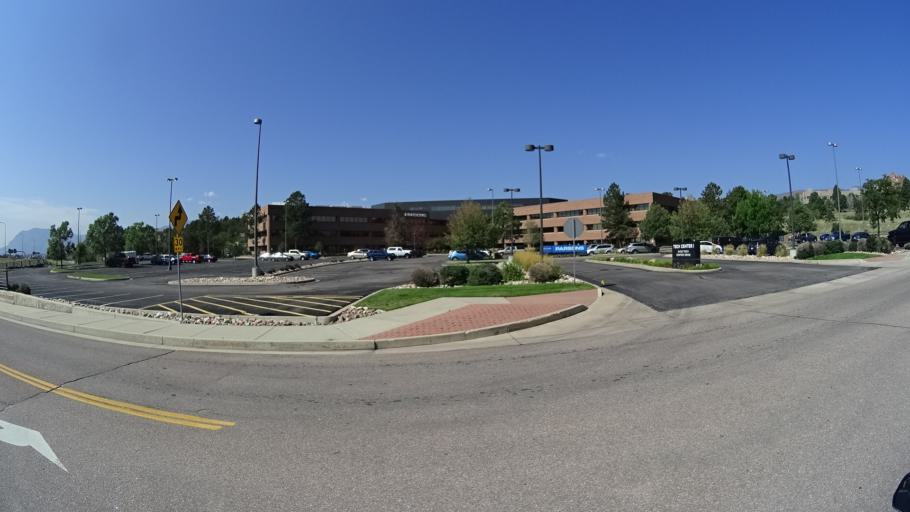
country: US
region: Colorado
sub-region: El Paso County
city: Colorado Springs
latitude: 38.9104
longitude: -104.8255
